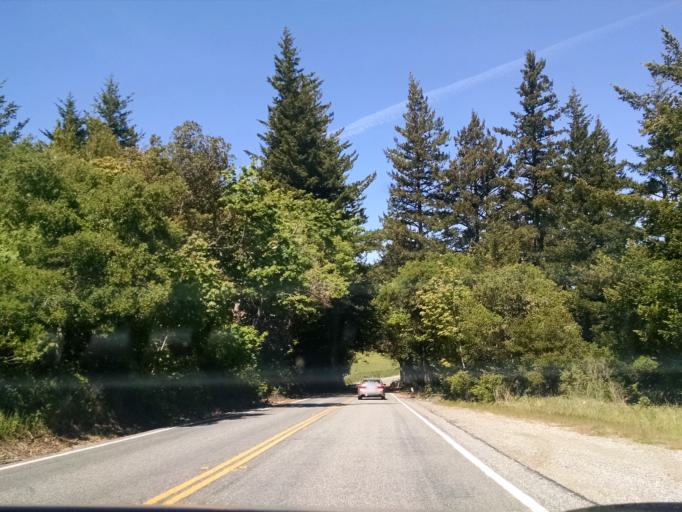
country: US
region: California
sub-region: San Mateo County
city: Portola Valley
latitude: 37.3504
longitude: -122.2377
